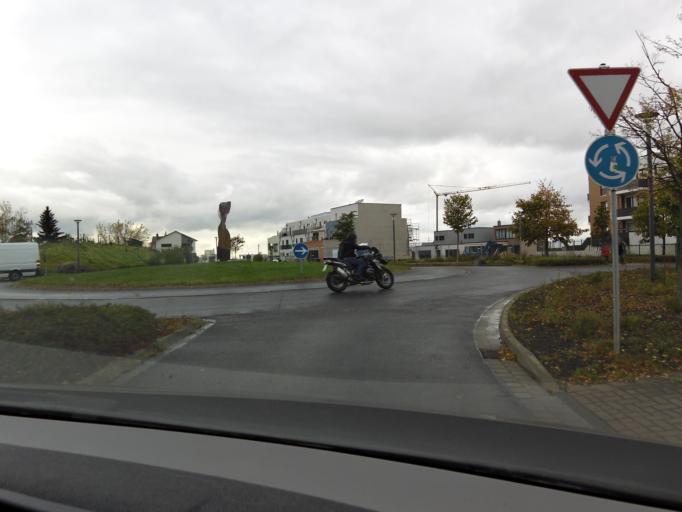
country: DE
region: Saxony
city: Zwenkau
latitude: 51.2320
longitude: 12.3334
